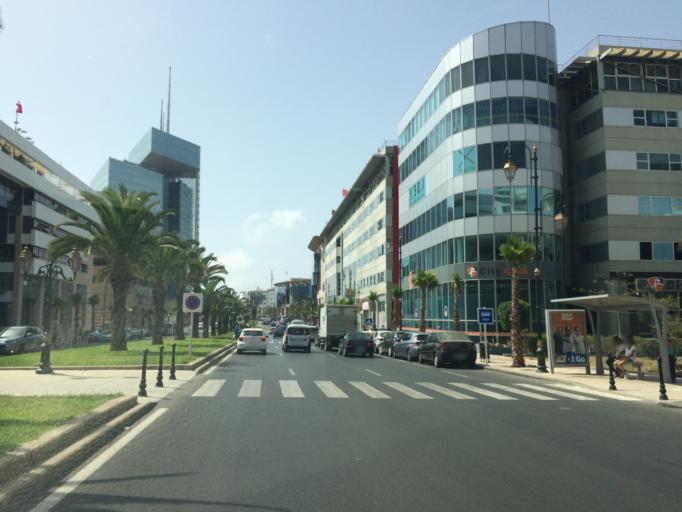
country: MA
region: Rabat-Sale-Zemmour-Zaer
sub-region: Skhirate-Temara
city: Temara
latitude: 33.9567
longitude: -6.8679
